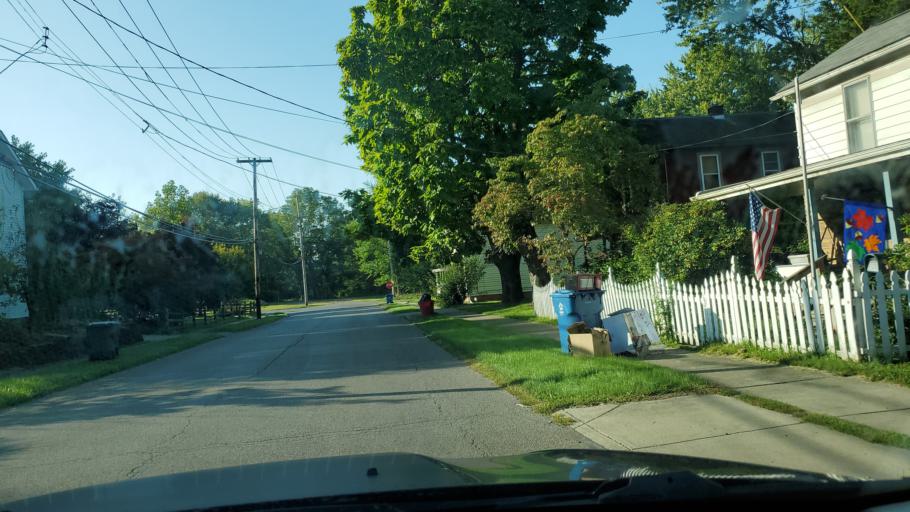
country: US
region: Ohio
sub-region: Trumbull County
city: Niles
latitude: 41.1742
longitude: -80.7515
